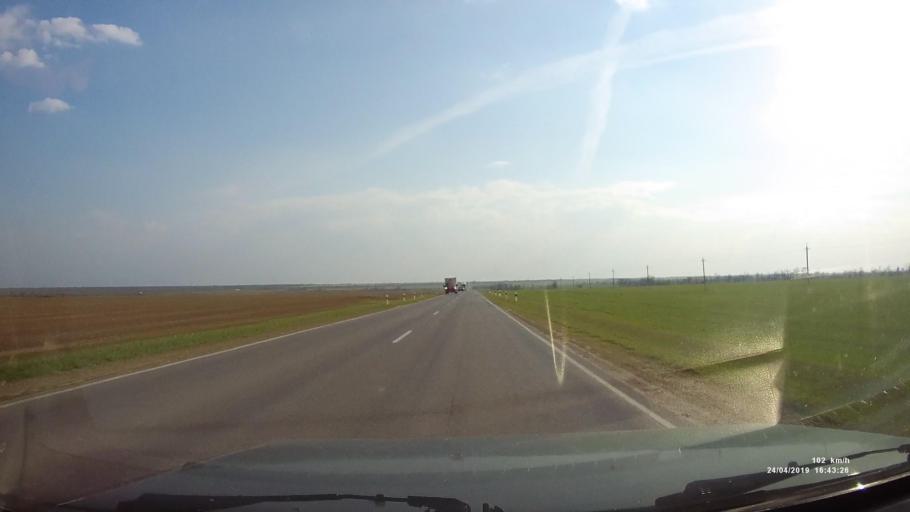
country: RU
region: Rostov
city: Gundorovskiy
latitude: 46.7945
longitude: 41.8405
